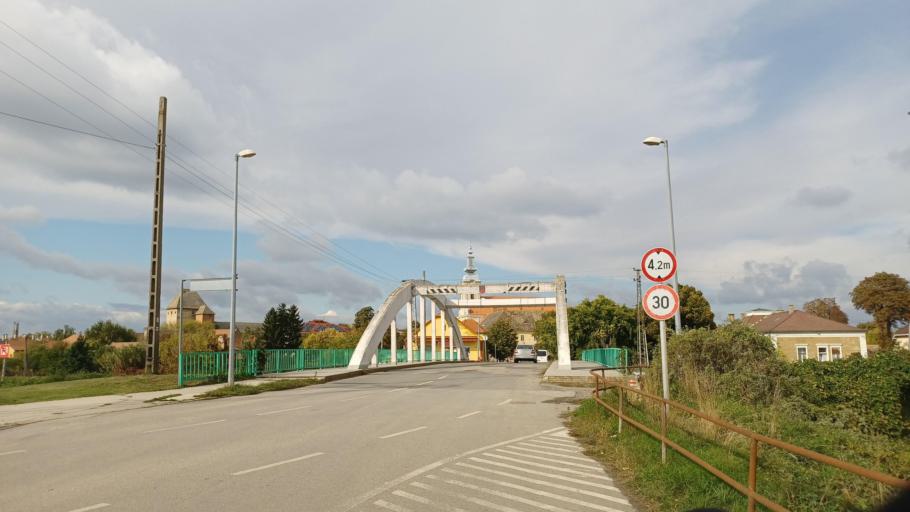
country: HU
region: Tolna
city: Simontornya
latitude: 46.7510
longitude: 18.5549
